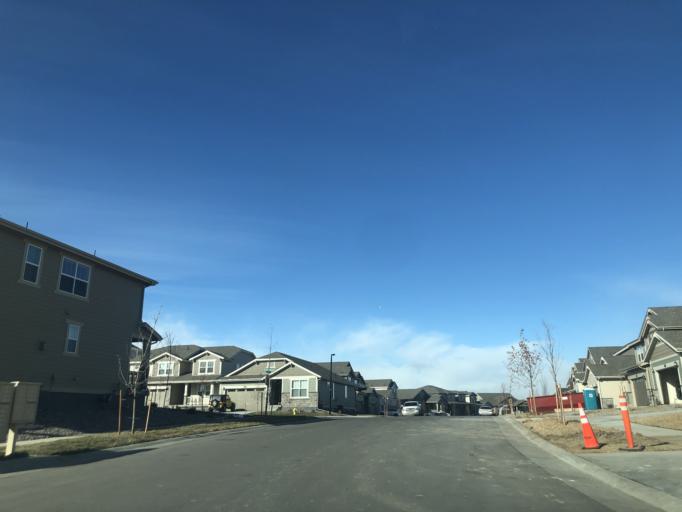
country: US
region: Colorado
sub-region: Douglas County
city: Stonegate
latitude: 39.5567
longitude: -104.8052
